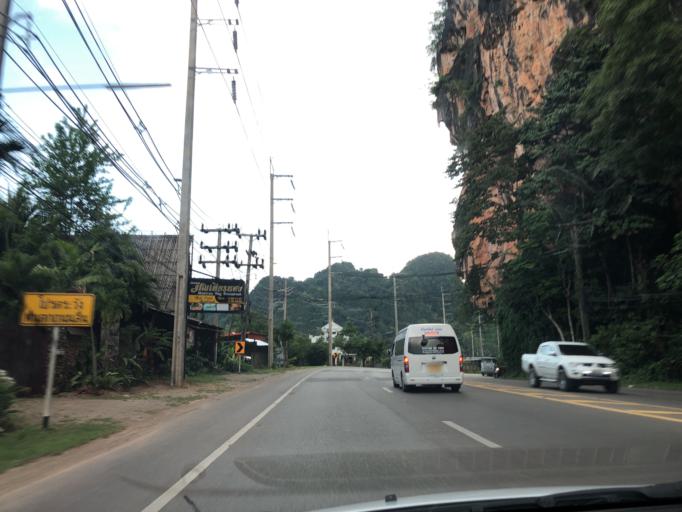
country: TH
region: Krabi
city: Krabi
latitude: 8.0867
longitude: 98.8784
